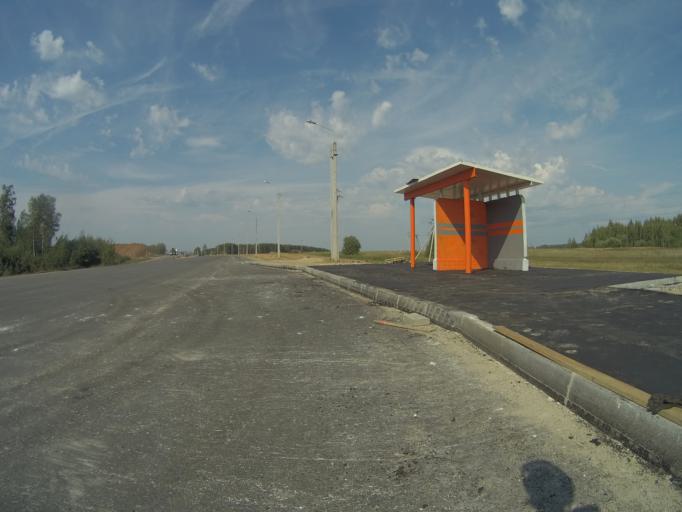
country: RU
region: Vladimir
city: Kommunar
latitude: 56.0696
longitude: 40.4974
